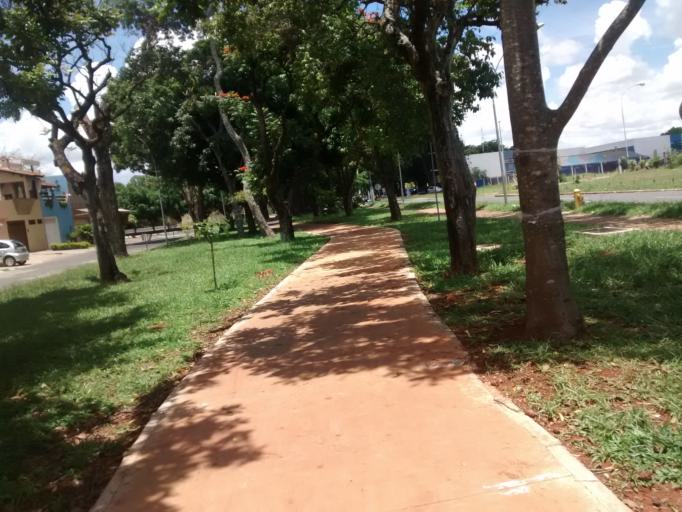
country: BR
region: Federal District
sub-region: Brasilia
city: Brasilia
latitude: -15.8015
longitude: -47.8980
